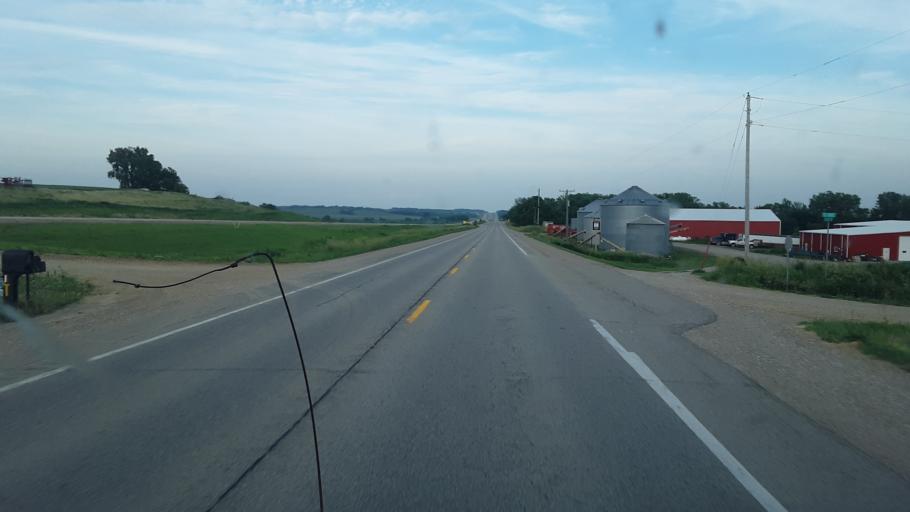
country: US
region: Iowa
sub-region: Tama County
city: Tama
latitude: 41.9638
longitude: -92.5033
